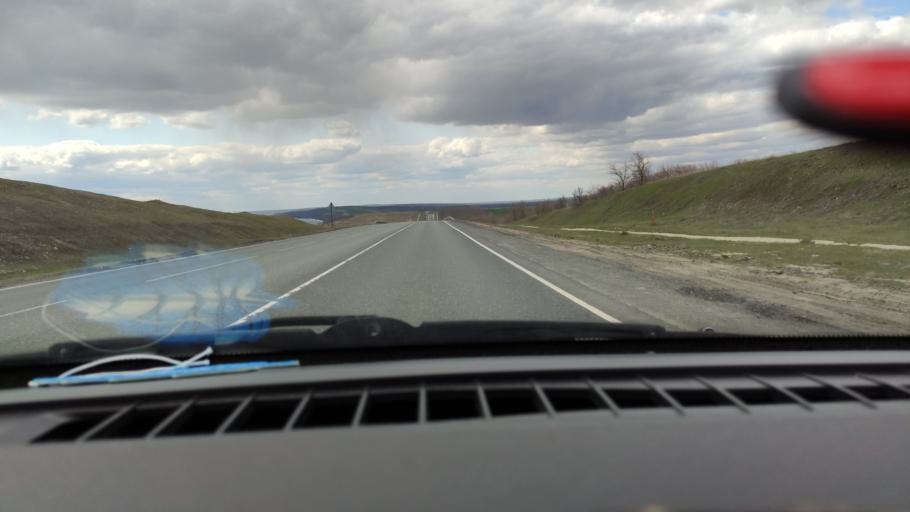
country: RU
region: Saratov
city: Alekseyevka
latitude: 52.2167
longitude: 47.8904
